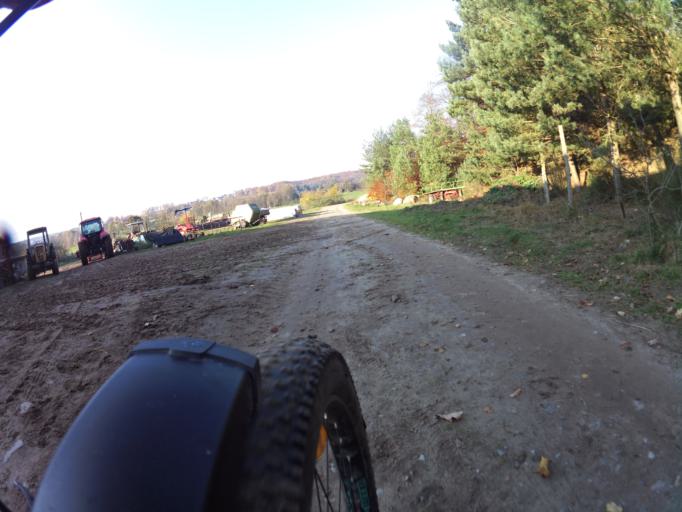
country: PL
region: Pomeranian Voivodeship
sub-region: Powiat pucki
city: Krokowa
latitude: 54.7468
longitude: 18.1956
